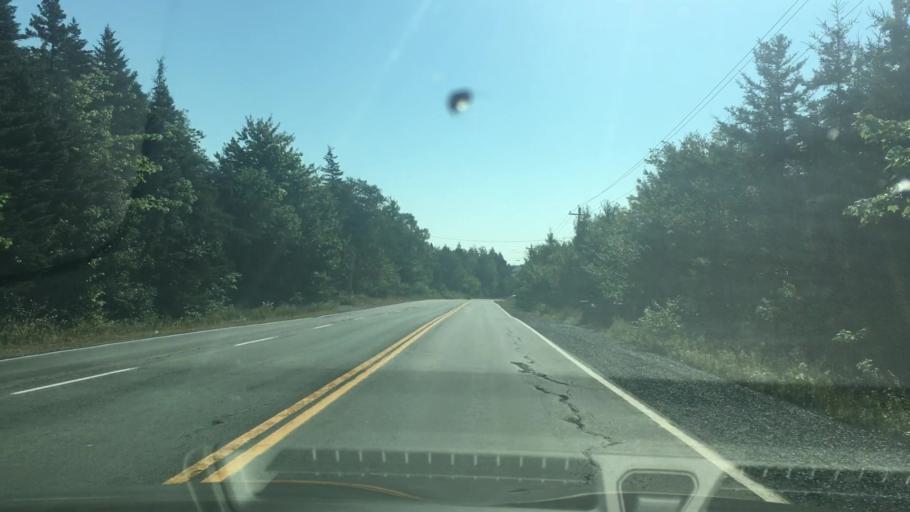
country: CA
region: Nova Scotia
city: Cole Harbour
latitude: 44.7783
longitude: -63.0762
